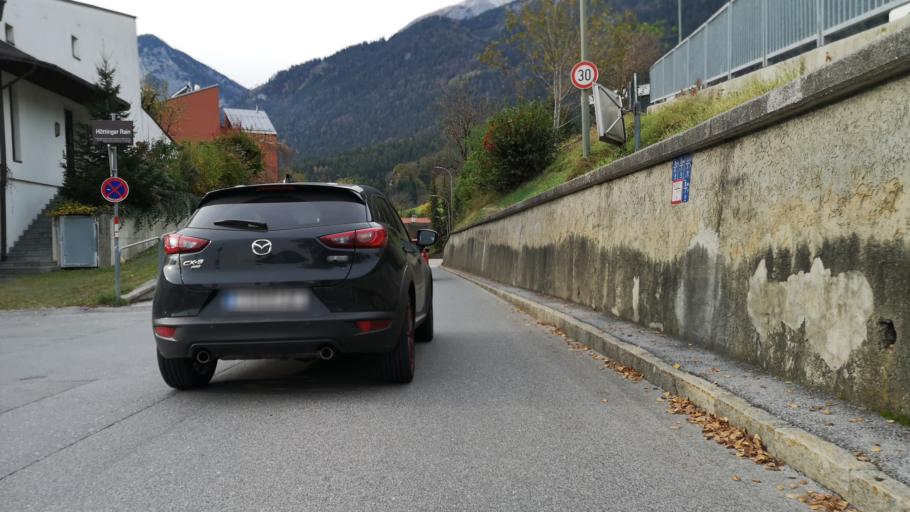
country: AT
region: Tyrol
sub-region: Innsbruck Stadt
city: Innsbruck
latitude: 47.2686
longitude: 11.3656
